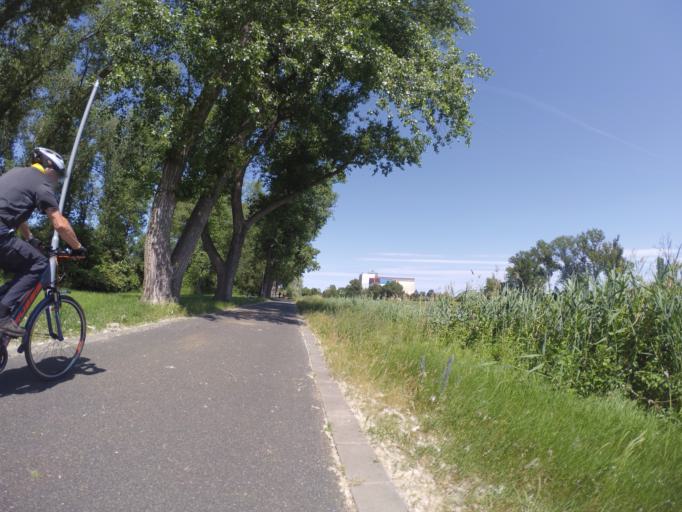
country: CZ
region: Central Bohemia
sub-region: Okres Nymburk
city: Nymburk
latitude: 50.1779
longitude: 15.0286
